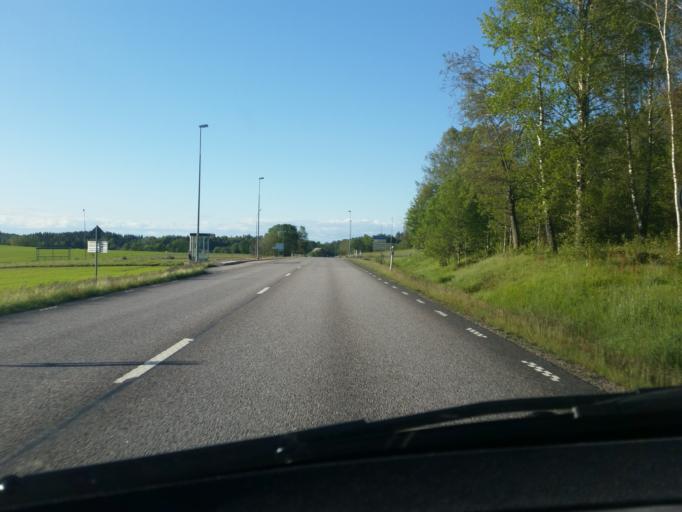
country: SE
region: Vaestra Goetaland
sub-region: Fargelanda Kommun
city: Faergelanda
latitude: 58.5414
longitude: 11.9880
